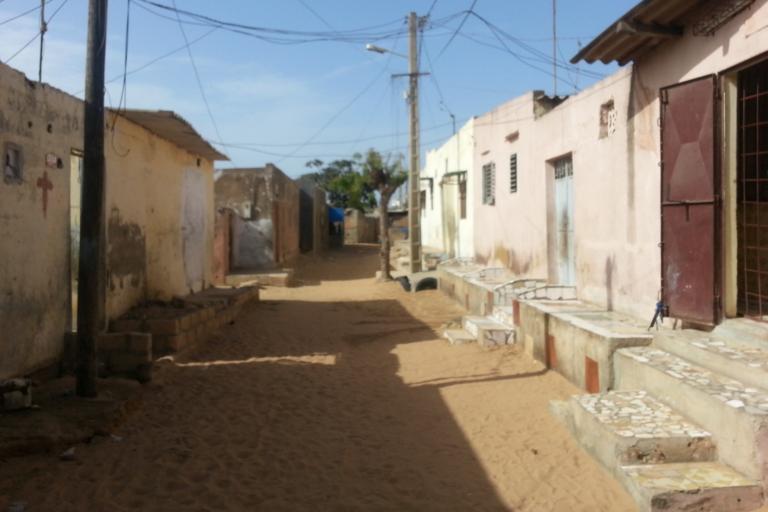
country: SN
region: Dakar
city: Pikine
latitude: 14.7723
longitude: -17.3820
